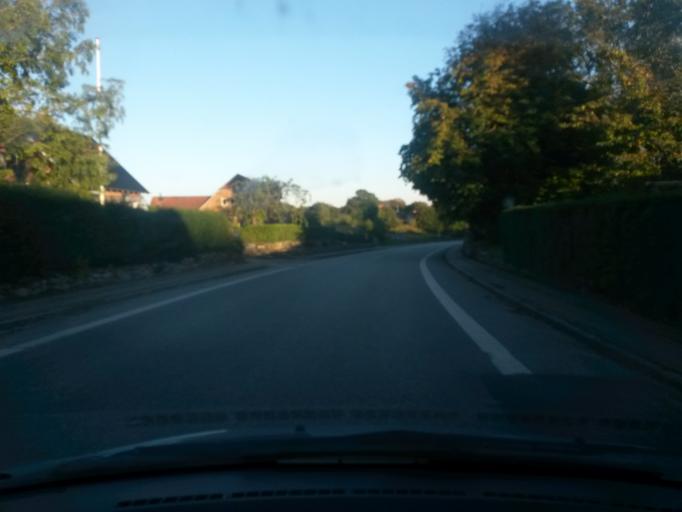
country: DK
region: Central Jutland
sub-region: Silkeborg Kommune
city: Kjellerup
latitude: 56.2875
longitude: 9.3230
